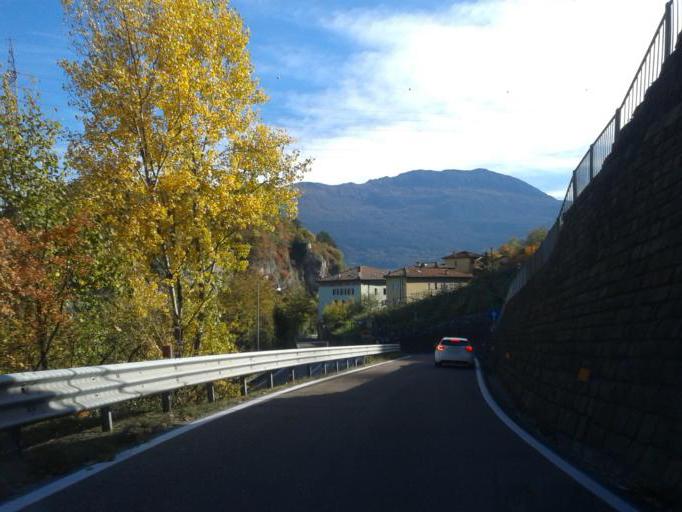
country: IT
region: Trentino-Alto Adige
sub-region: Provincia di Trento
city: Trento
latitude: 46.0740
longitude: 11.1039
